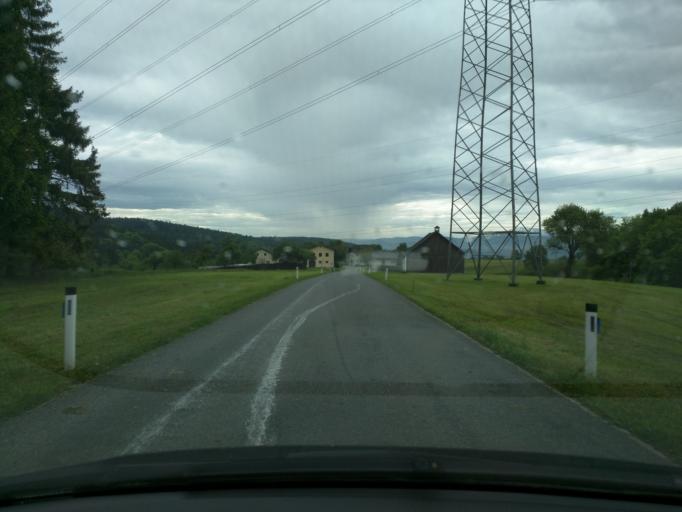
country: AT
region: Lower Austria
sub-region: Politischer Bezirk Melk
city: Blindenmarkt
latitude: 48.1482
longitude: 14.9818
